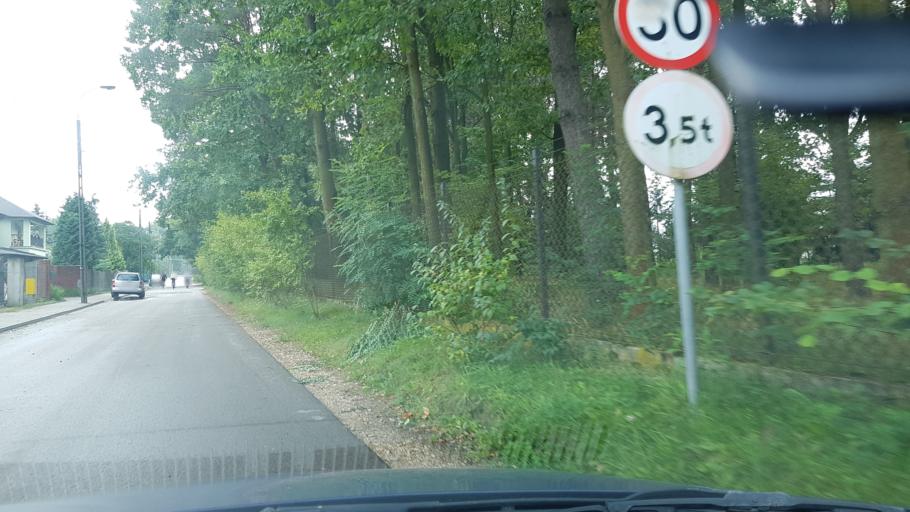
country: PL
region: Masovian Voivodeship
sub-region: Powiat piaseczynski
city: Konstancin-Jeziorna
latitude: 52.1052
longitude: 21.1003
